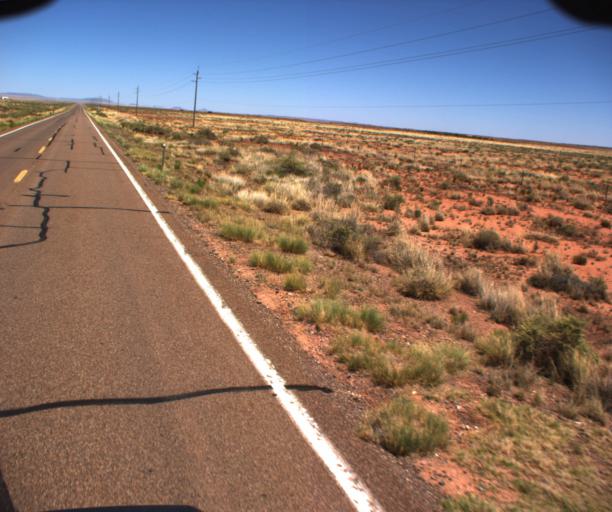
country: US
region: Arizona
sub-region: Coconino County
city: LeChee
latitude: 34.9522
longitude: -110.7591
